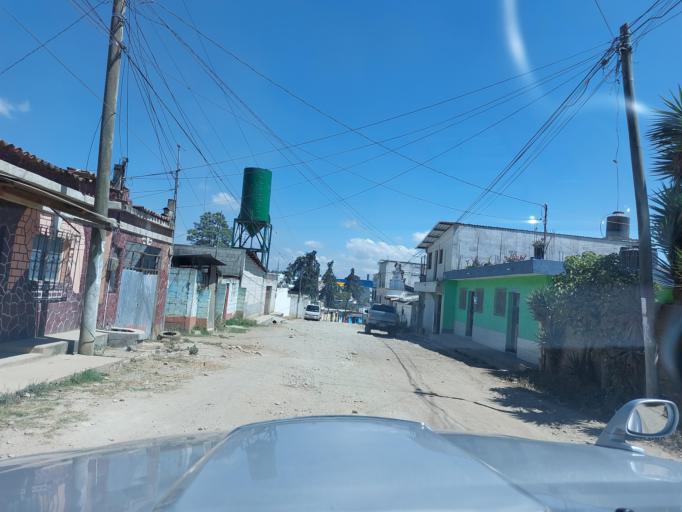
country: GT
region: Chimaltenango
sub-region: Municipio de Chimaltenango
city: Chimaltenango
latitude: 14.6551
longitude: -90.8306
